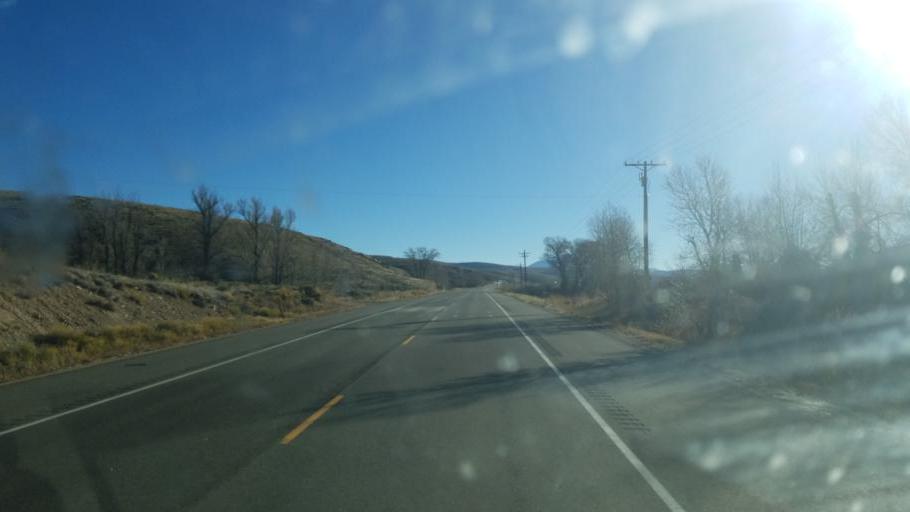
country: US
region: Colorado
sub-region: Gunnison County
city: Gunnison
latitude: 38.5243
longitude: -106.8011
